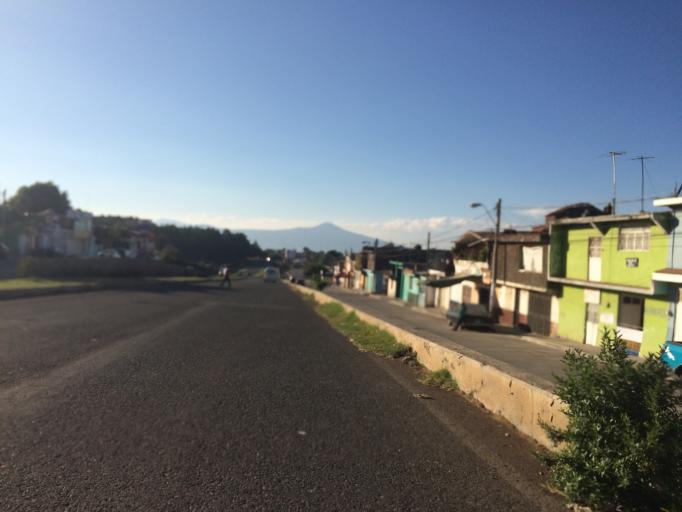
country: MX
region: Michoacan
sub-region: Patzcuaro
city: Colonia Vista Bella (Lomas del Peaje)
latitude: 19.5017
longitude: -101.6025
